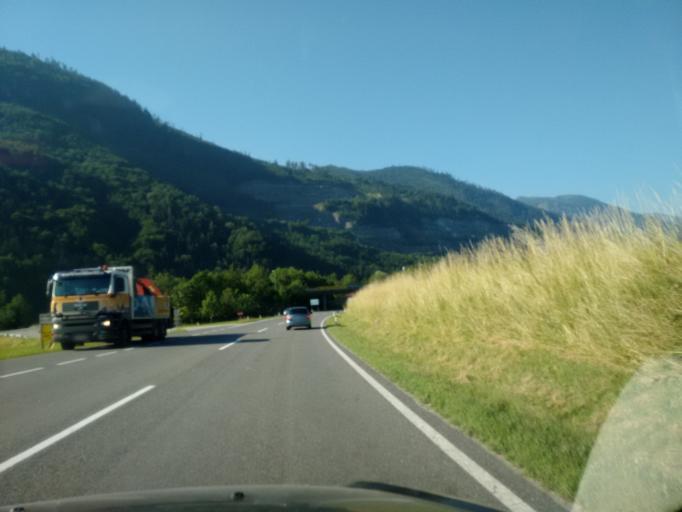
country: AT
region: Upper Austria
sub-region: Politischer Bezirk Gmunden
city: Ebensee
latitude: 47.8026
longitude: 13.7822
